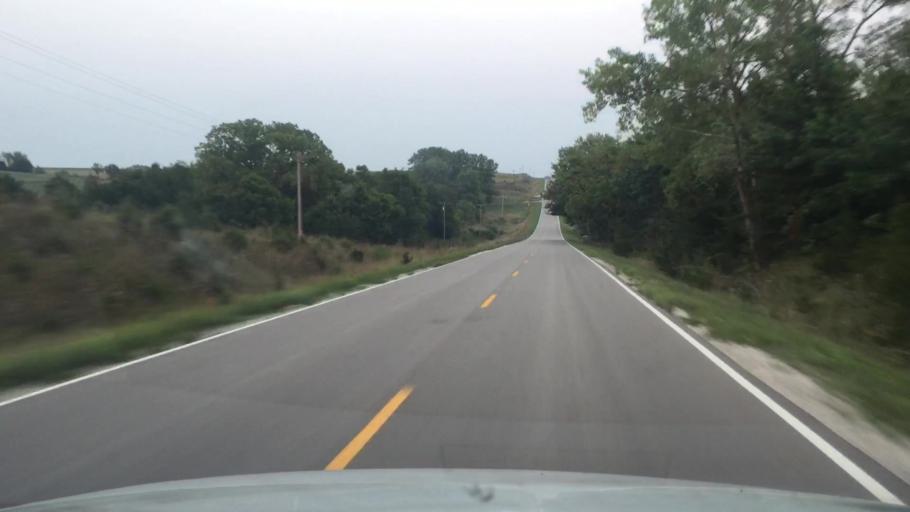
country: US
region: Iowa
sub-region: Warren County
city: Indianola
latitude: 41.1905
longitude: -93.5633
